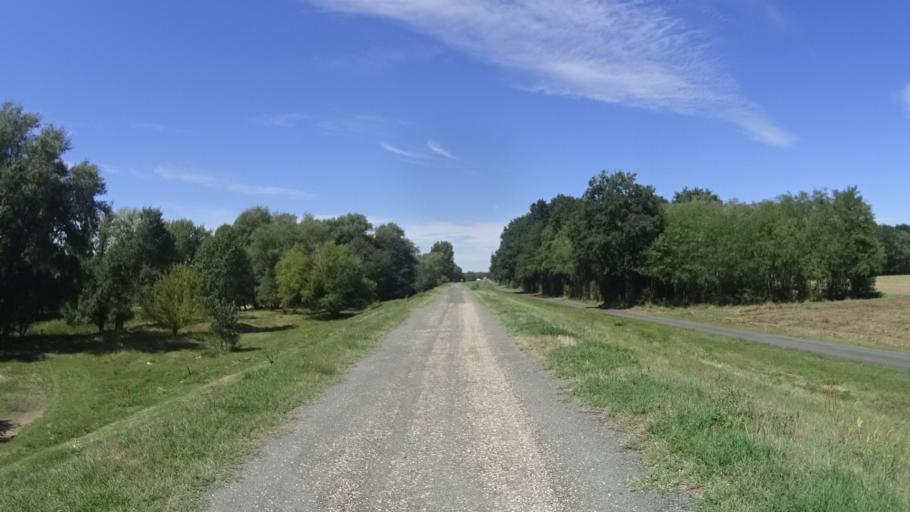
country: FR
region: Centre
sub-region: Departement du Loiret
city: Briare
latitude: 47.5933
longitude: 2.7730
